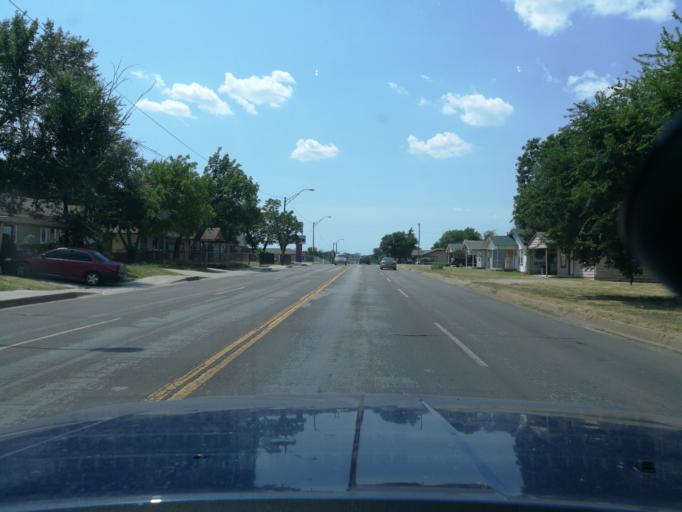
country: US
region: Oklahoma
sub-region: Oklahoma County
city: Oklahoma City
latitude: 35.4208
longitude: -97.5044
